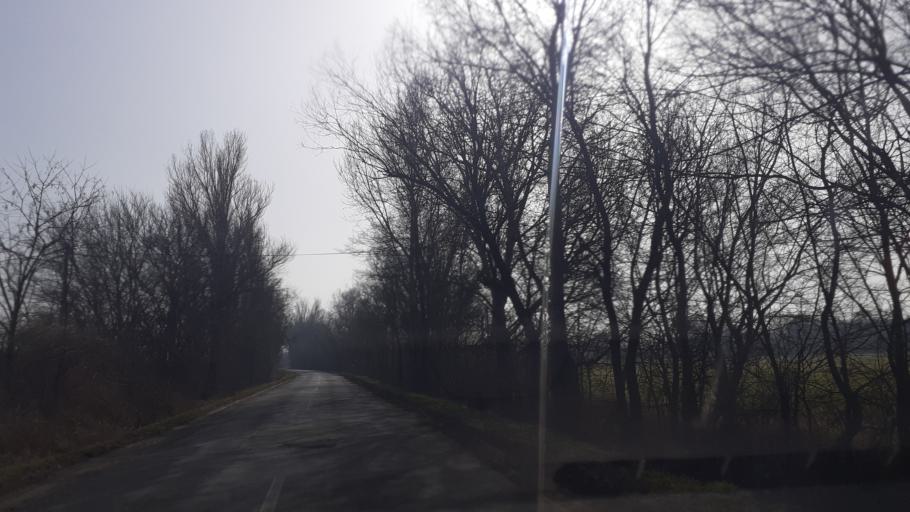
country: HU
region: Bacs-Kiskun
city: Kunszentmiklos
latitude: 47.0264
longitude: 19.2194
